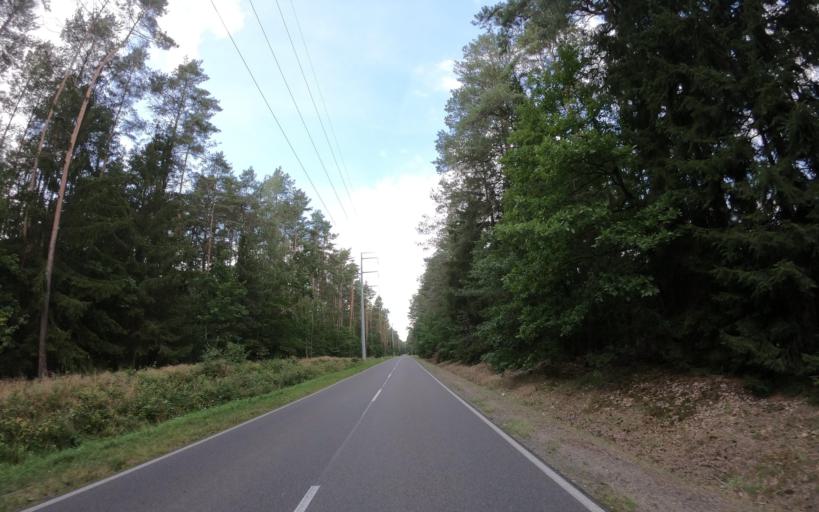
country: PL
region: West Pomeranian Voivodeship
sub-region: Powiat drawski
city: Czaplinek
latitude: 53.4955
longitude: 16.2244
